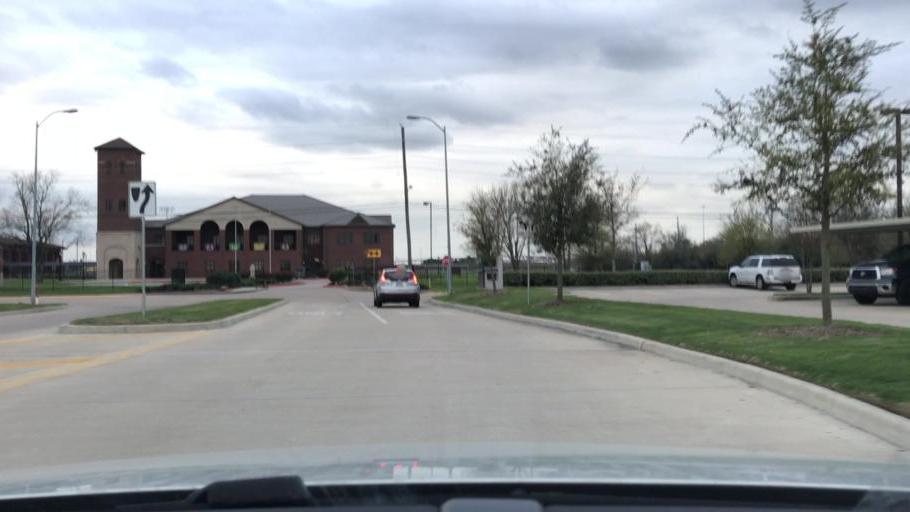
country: US
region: Texas
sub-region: Harris County
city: Katy
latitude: 29.8025
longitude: -95.7725
